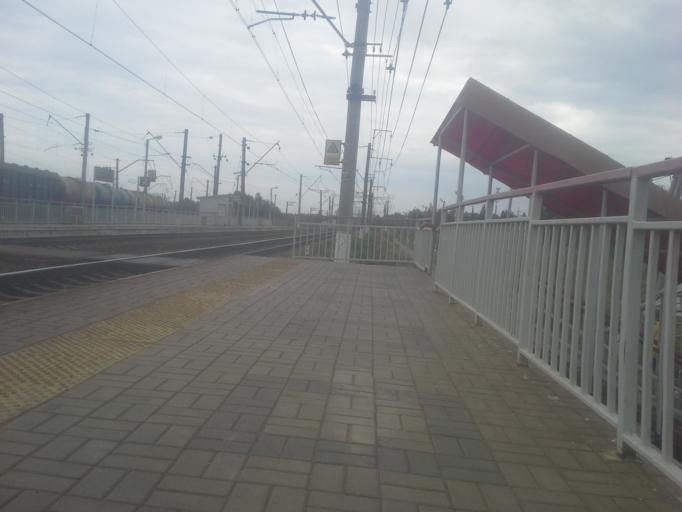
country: RU
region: Moskovskaya
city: Kievskij
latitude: 55.4249
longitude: 36.8654
